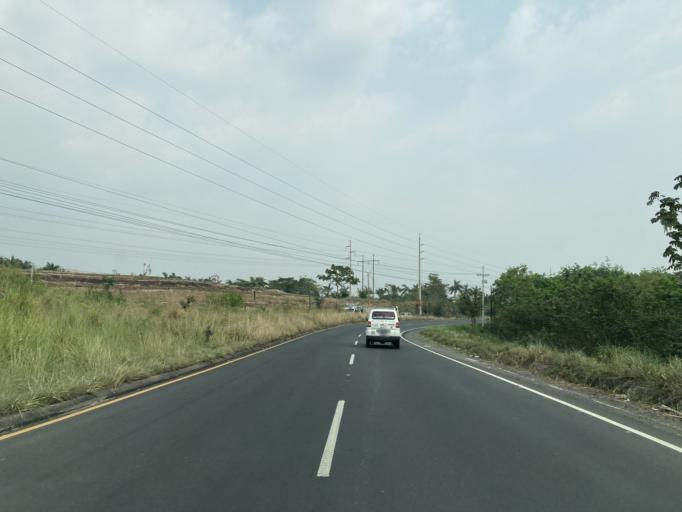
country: GT
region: Suchitepeque
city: Patulul
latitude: 14.3655
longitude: -91.1003
